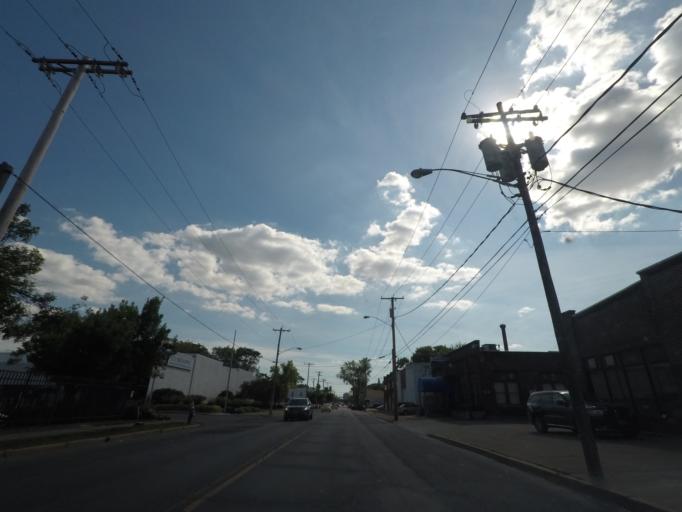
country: US
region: New York
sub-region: Albany County
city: Menands
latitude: 42.6745
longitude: -73.7367
